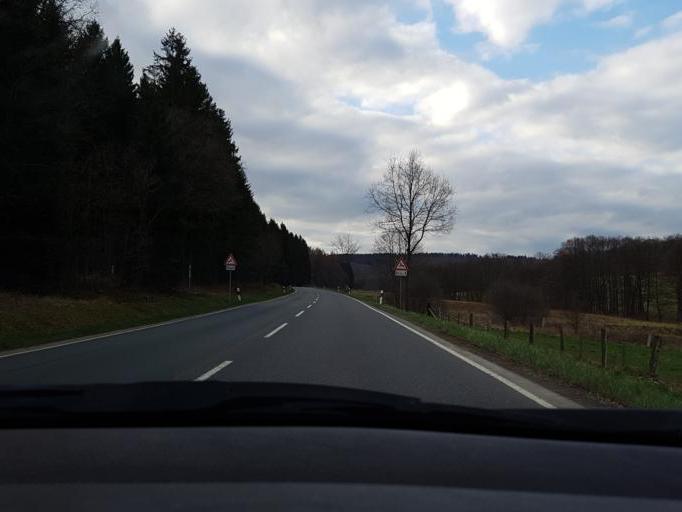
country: DE
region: Lower Saxony
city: Bodenfelde
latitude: 51.7199
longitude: 9.5219
